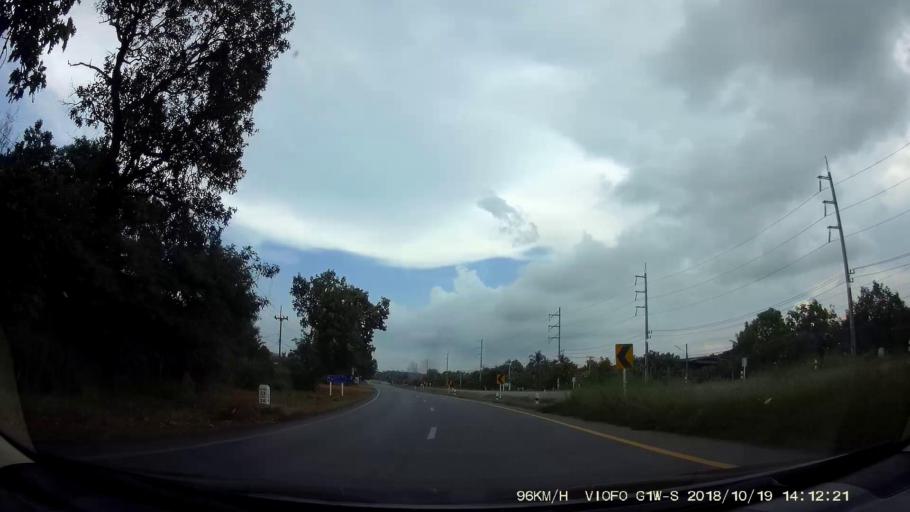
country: TH
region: Chaiyaphum
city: Khon Sawan
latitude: 15.9468
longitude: 102.1725
